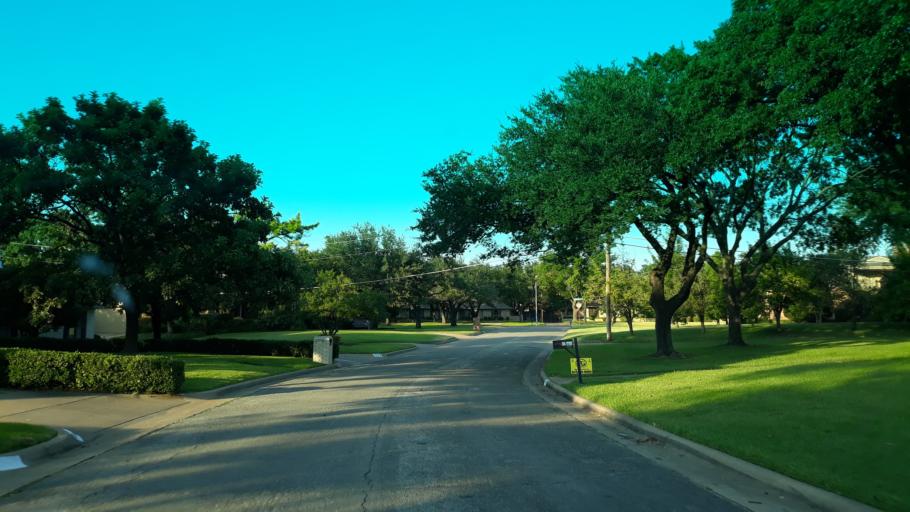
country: US
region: Texas
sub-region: Dallas County
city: Addison
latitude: 32.9426
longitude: -96.7908
